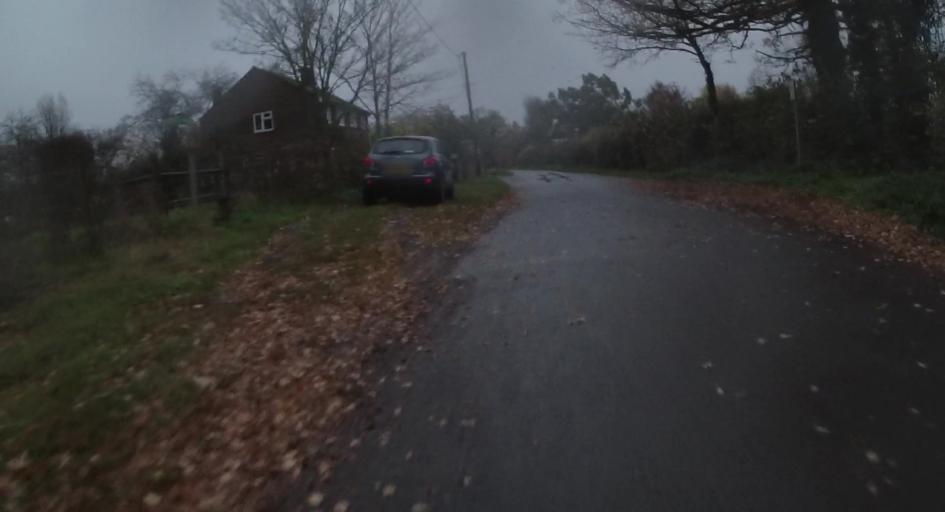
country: GB
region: England
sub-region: Wokingham
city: Swallowfield
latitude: 51.3715
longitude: -0.9525
